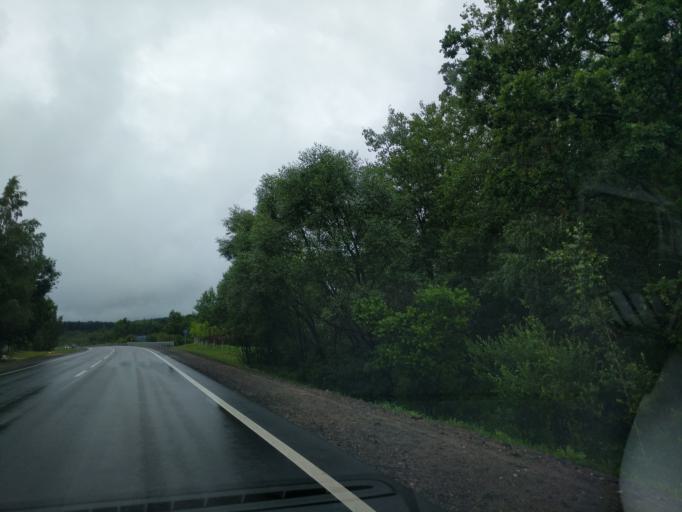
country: BY
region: Minsk
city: Syomkava
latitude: 54.1787
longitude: 27.5003
